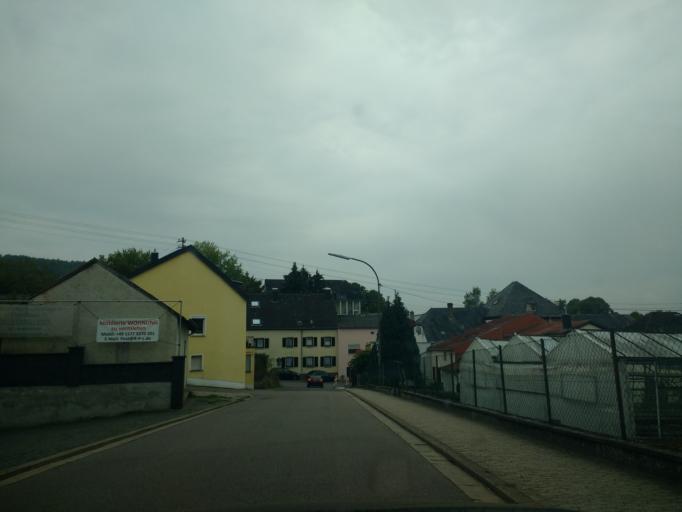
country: DE
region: Saarland
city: Perl
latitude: 49.4732
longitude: 6.3888
